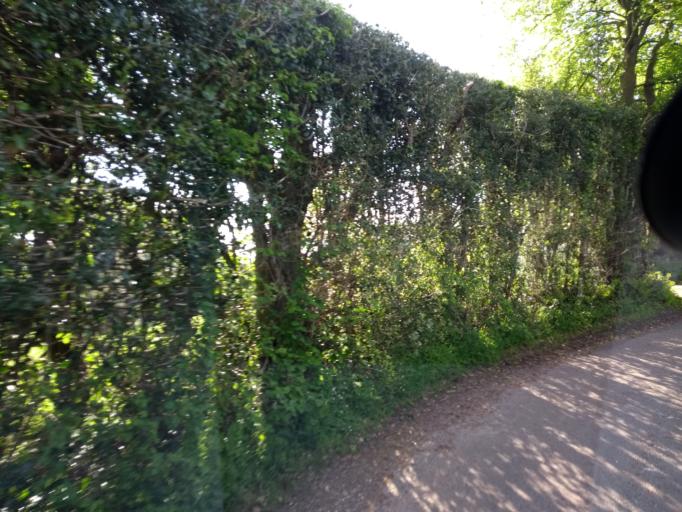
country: GB
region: England
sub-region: Dorset
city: Lyme Regis
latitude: 50.7938
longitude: -2.8868
